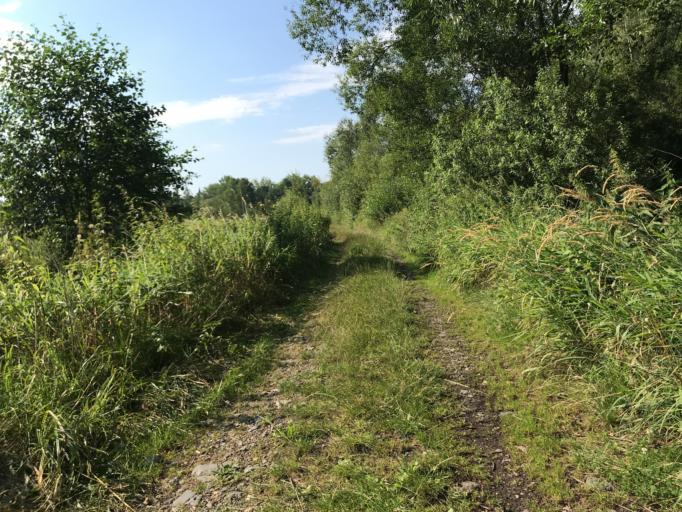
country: CZ
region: Jihocesky
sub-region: Okres Jindrichuv Hradec
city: Trebon
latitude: 49.0136
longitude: 14.7639
